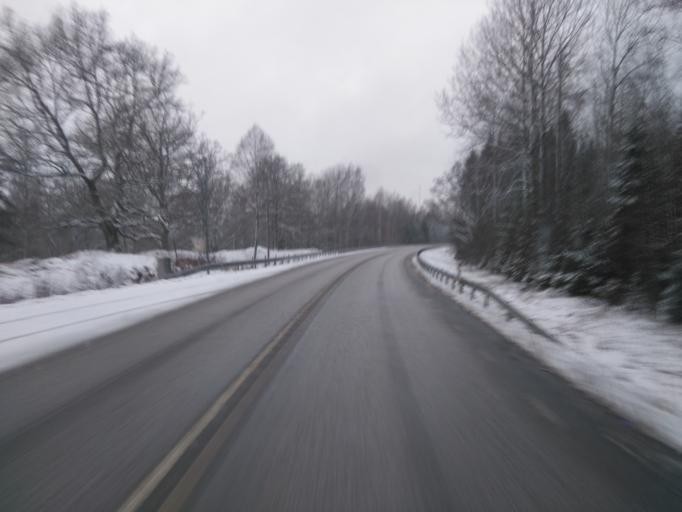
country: SE
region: Joenkoeping
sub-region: Eksjo Kommun
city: Eksjoe
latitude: 57.6439
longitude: 15.0652
